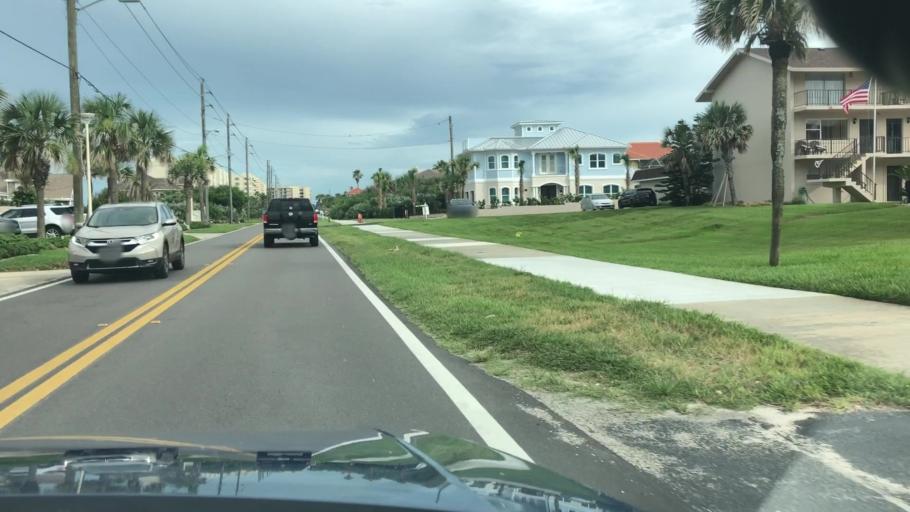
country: US
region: Florida
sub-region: Volusia County
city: Ponce Inlet
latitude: 29.1124
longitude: -80.9465
